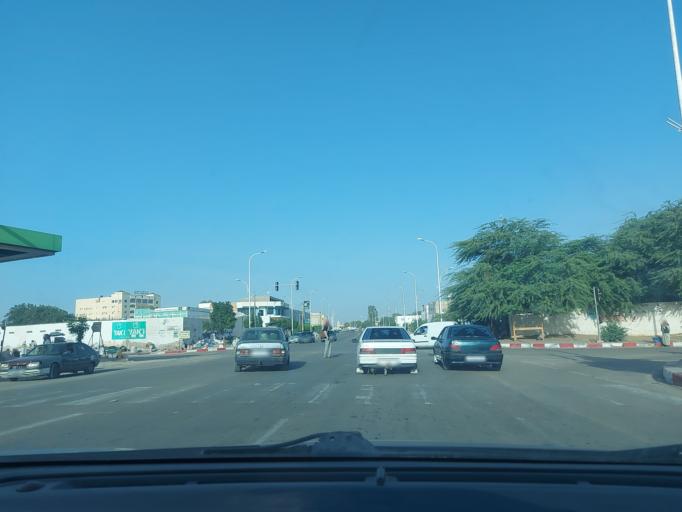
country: MR
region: Nouakchott
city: Nouakchott
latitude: 18.0877
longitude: -15.9823
